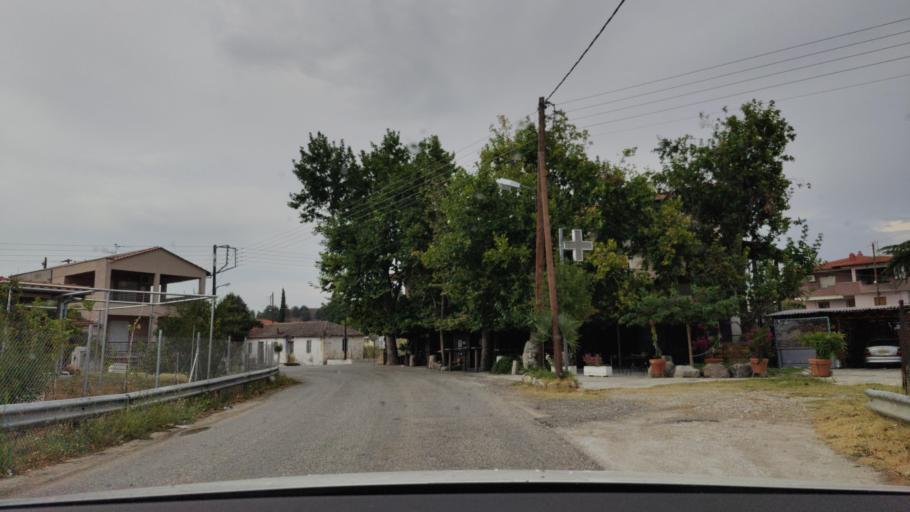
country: GR
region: Central Macedonia
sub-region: Nomos Serron
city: Lefkonas
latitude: 41.1192
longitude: 23.4608
